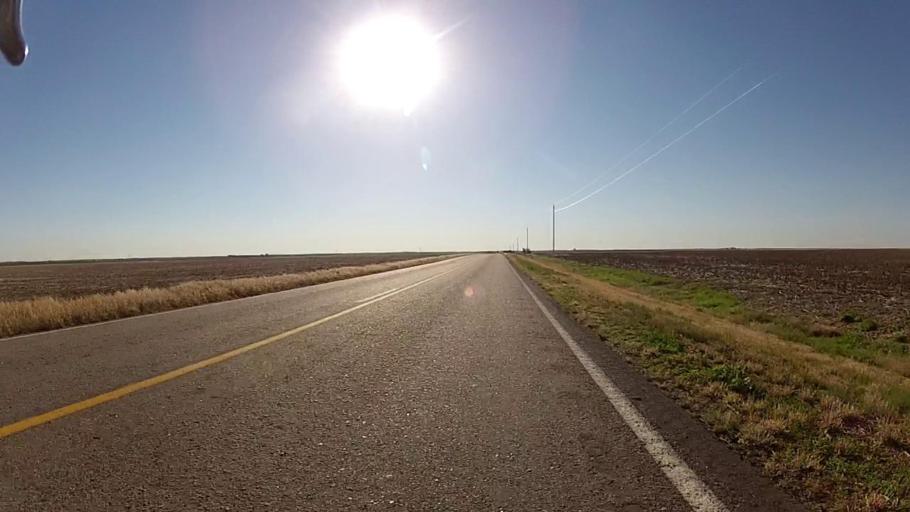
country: US
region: Kansas
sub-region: Ford County
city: Dodge City
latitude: 37.6463
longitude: -99.8385
